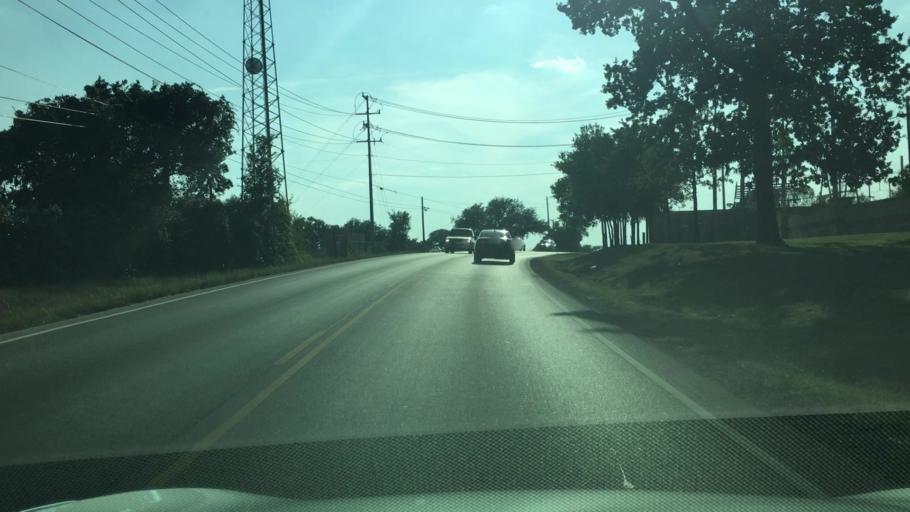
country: US
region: Texas
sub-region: Hays County
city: Dripping Springs
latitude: 30.1171
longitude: -97.9844
